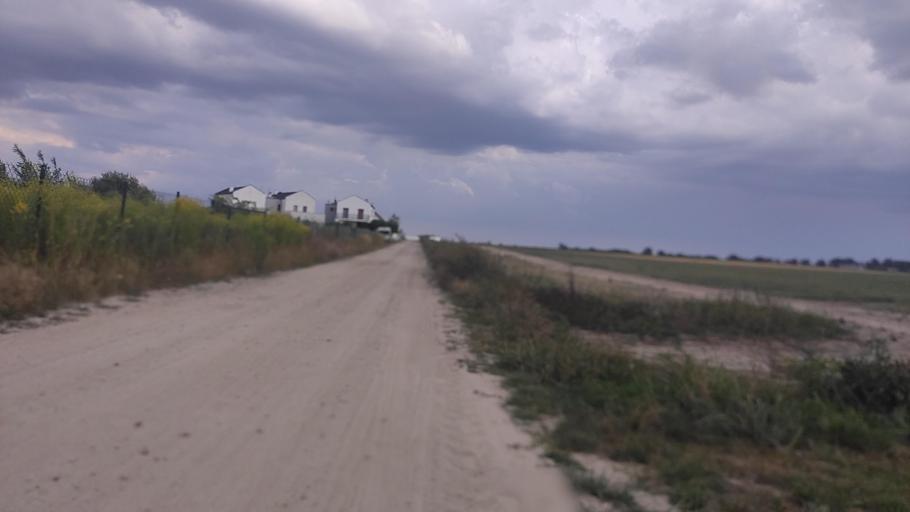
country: PL
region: Greater Poland Voivodeship
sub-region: Powiat poznanski
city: Swarzedz
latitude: 52.4238
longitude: 17.1134
